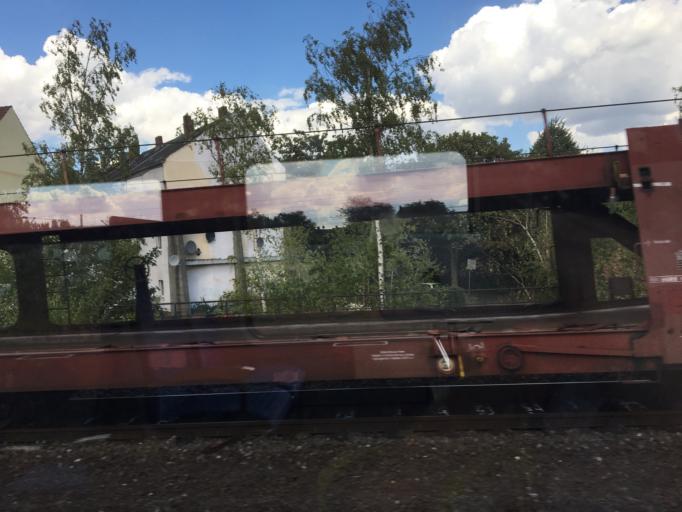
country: DE
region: North Rhine-Westphalia
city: Witten
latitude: 51.4789
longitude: 7.3011
